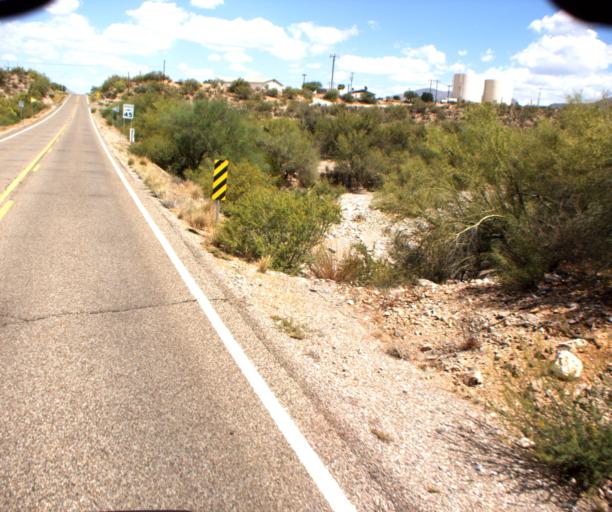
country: US
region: Arizona
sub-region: Pinal County
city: Kearny
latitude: 33.0562
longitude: -110.9011
